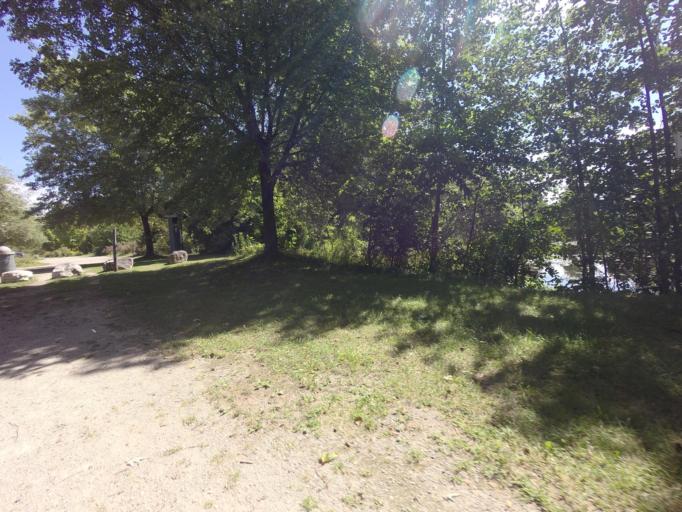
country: CA
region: Ontario
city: Orangeville
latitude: 43.7850
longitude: -80.1446
